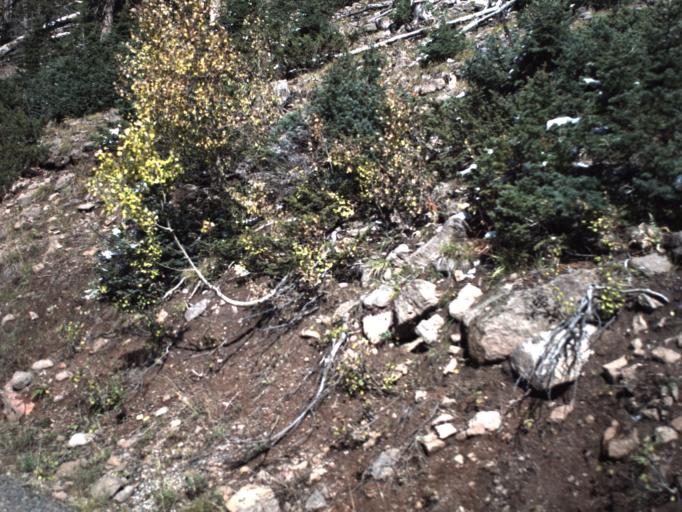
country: US
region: Utah
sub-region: Piute County
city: Junction
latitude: 38.3098
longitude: -112.3638
